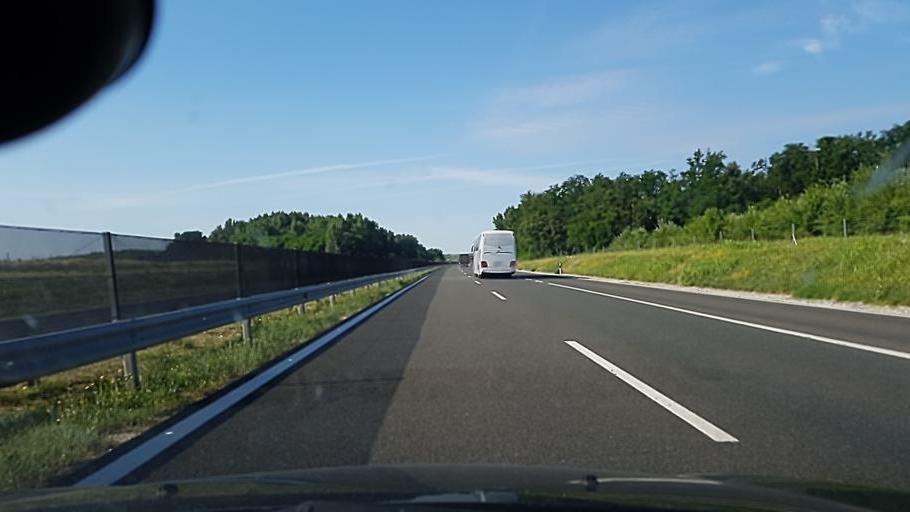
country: HU
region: Fejer
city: Baracs
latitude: 46.8529
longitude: 18.8747
